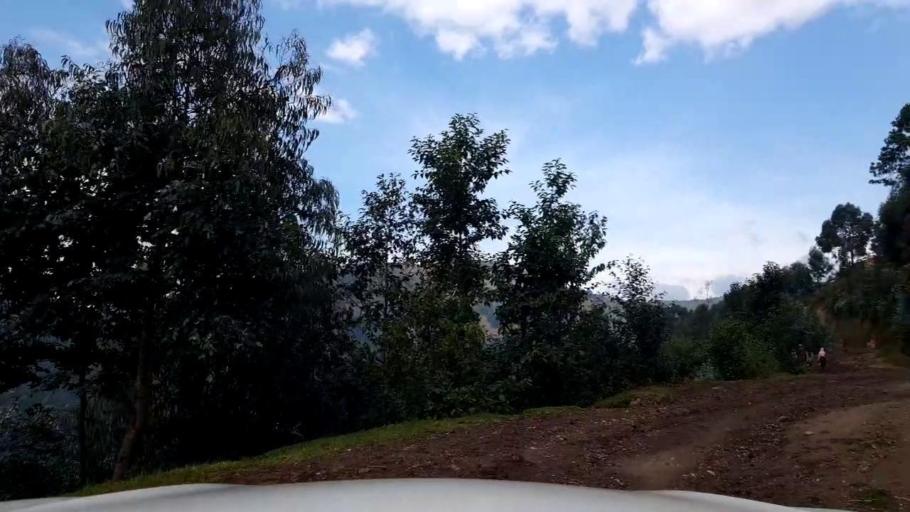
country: RW
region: Western Province
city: Gisenyi
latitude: -1.7174
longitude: 29.3882
